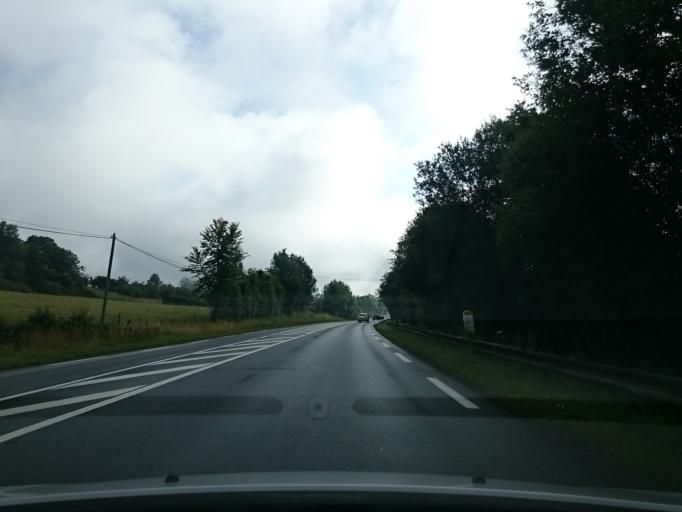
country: FR
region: Lower Normandy
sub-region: Departement du Calvados
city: Cambremer
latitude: 49.1304
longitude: 0.1119
